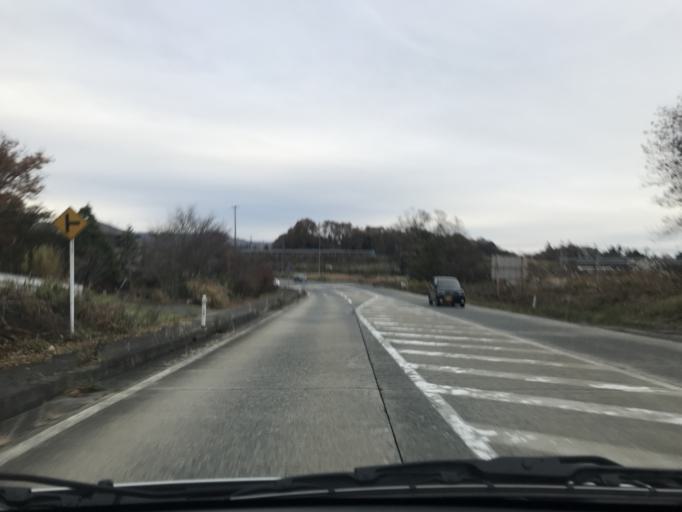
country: JP
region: Iwate
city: Kitakami
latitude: 39.2881
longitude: 141.2179
